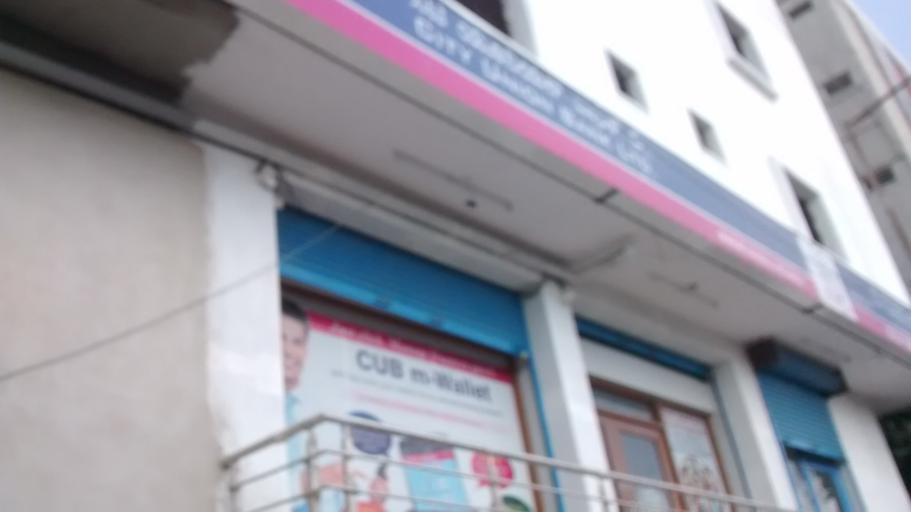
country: IN
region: Karnataka
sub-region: Bangalore Urban
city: Bangalore
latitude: 12.9583
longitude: 77.7016
